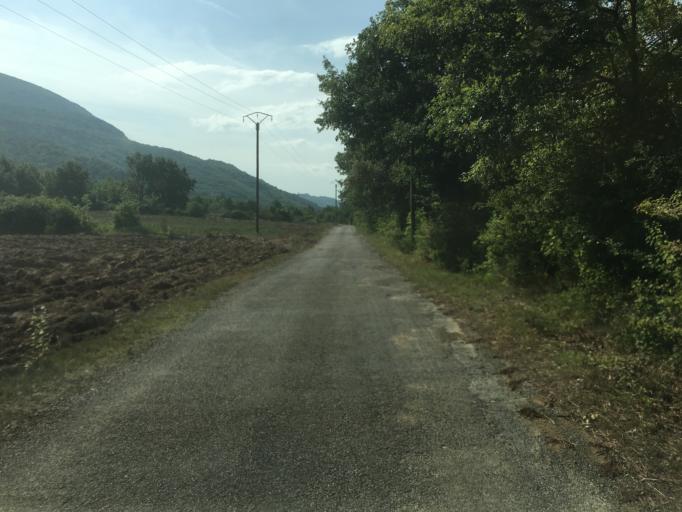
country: FR
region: Provence-Alpes-Cote d'Azur
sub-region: Departement des Alpes-de-Haute-Provence
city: Mallemoisson
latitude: 43.9339
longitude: 6.1873
